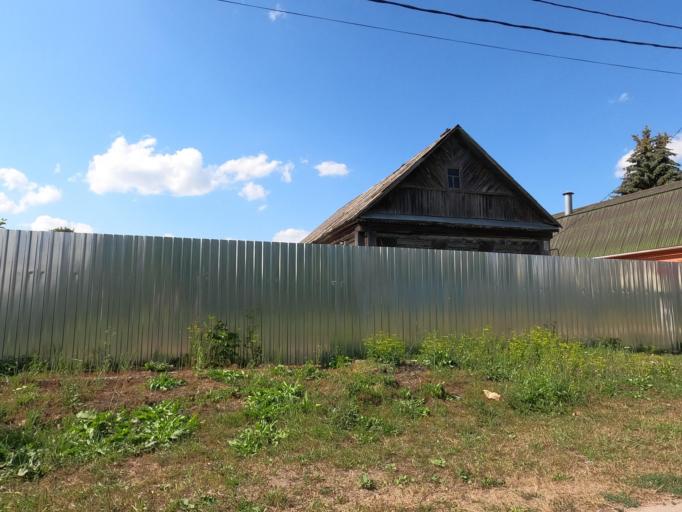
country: RU
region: Moskovskaya
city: Peski
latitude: 55.2301
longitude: 38.7464
